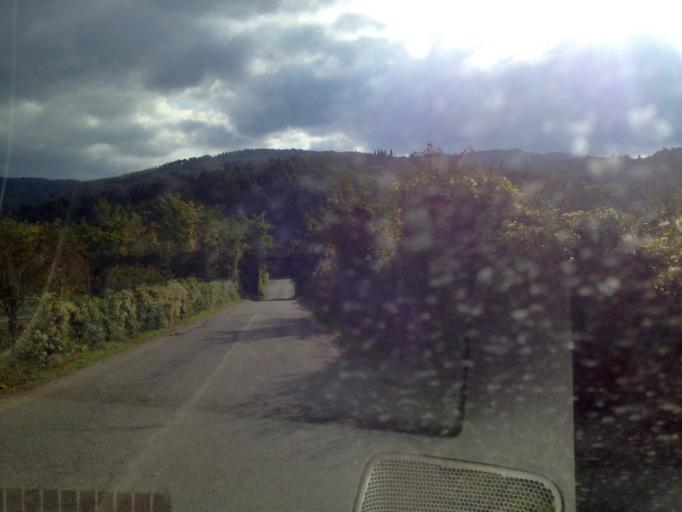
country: IT
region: Tuscany
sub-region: Province of Florence
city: Montebonello
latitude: 43.8508
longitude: 11.5037
